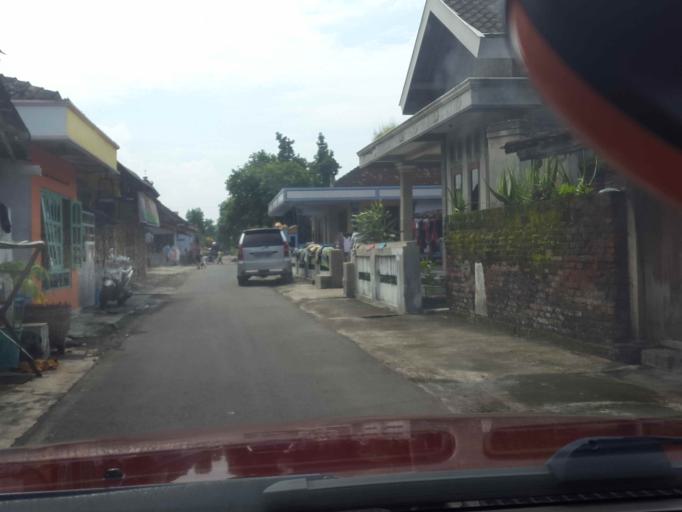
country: ID
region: Central Java
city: Jaten
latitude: -7.6008
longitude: 110.9432
